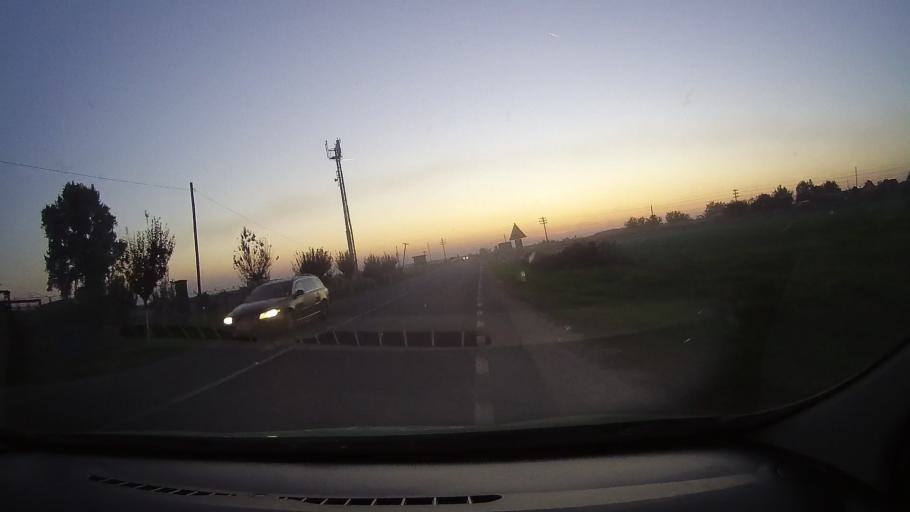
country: RO
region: Bihor
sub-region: Comuna Simian
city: Simian
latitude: 47.5111
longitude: 22.1150
